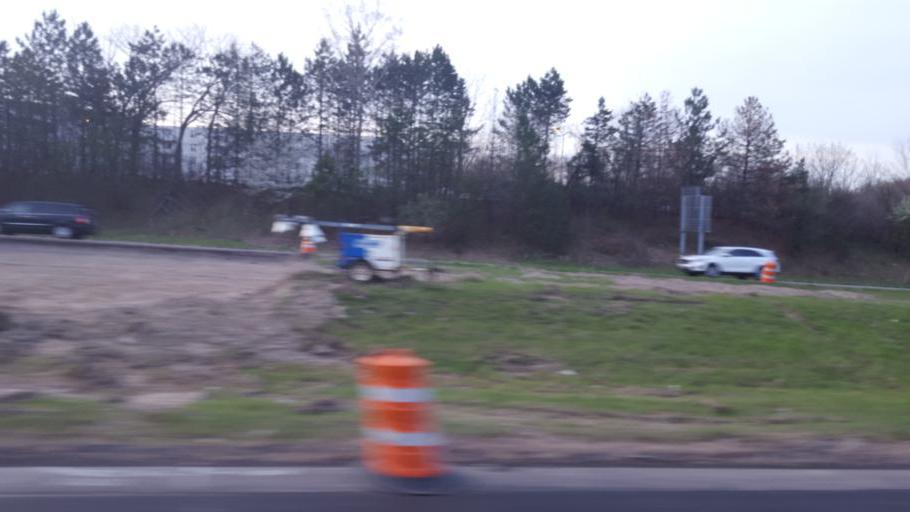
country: US
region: Ohio
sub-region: Lorain County
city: Sheffield
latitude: 41.4055
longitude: -82.1063
